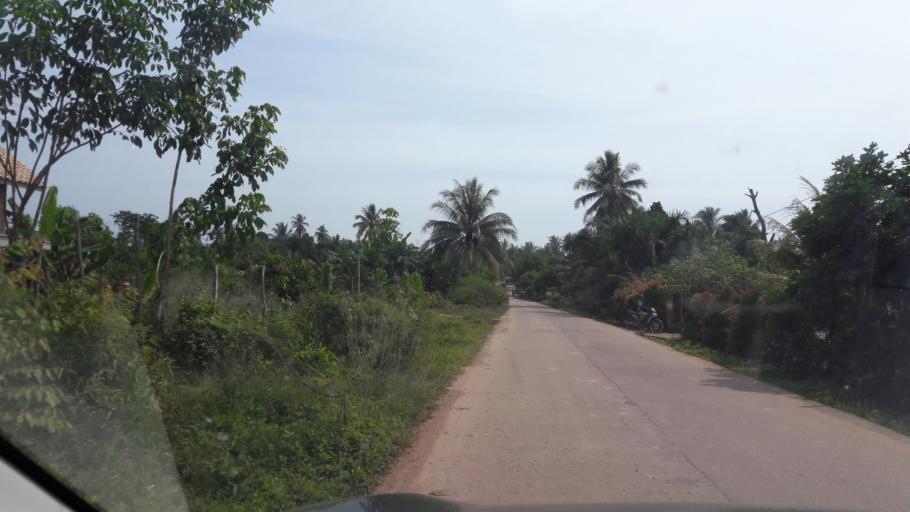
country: ID
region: South Sumatra
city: Gunungmenang
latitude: -3.3140
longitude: 104.1135
